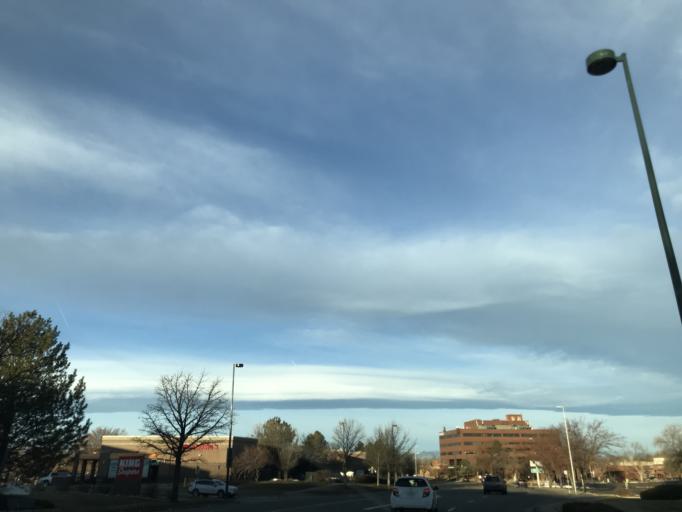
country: US
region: Colorado
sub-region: Arapahoe County
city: Cherry Hills Village
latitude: 39.6675
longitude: -104.9365
